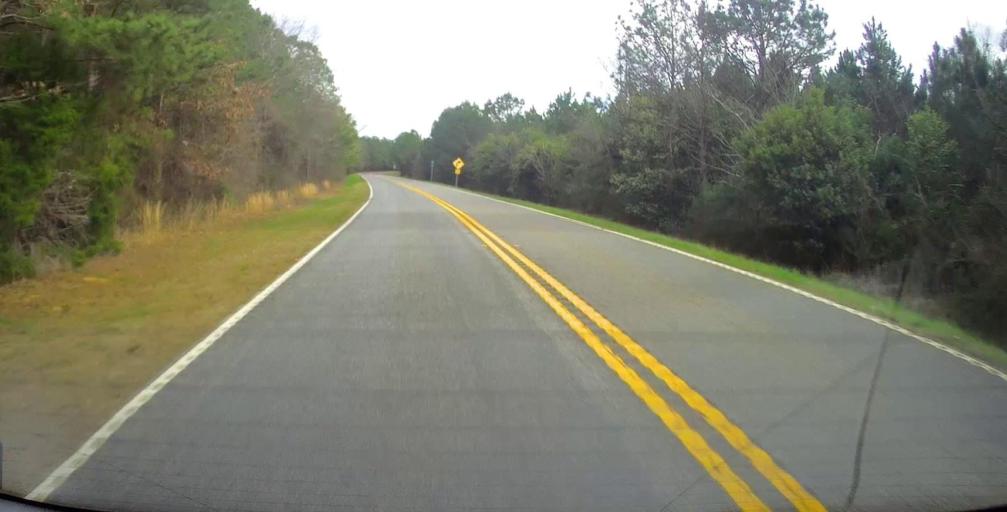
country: US
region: Georgia
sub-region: Marion County
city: Buena Vista
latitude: 32.4351
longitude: -84.4314
